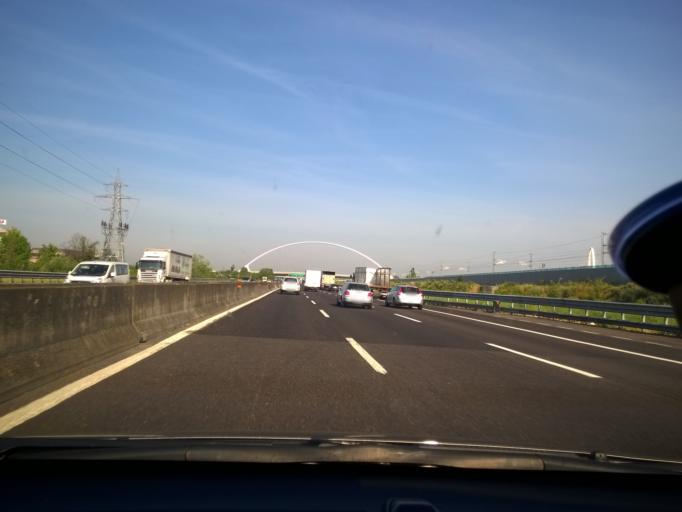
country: IT
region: Emilia-Romagna
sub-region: Provincia di Reggio Emilia
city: Reggio nell'Emilia
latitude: 44.7258
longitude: 10.6449
